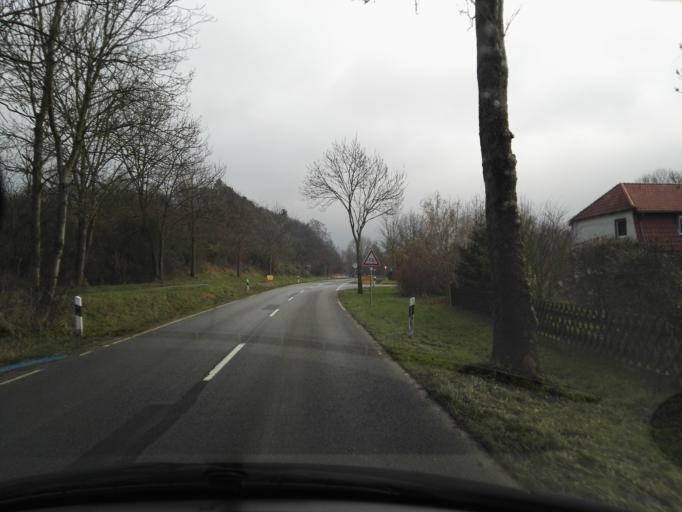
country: DE
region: Lower Saxony
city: Eberholzen
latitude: 52.0827
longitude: 9.8433
